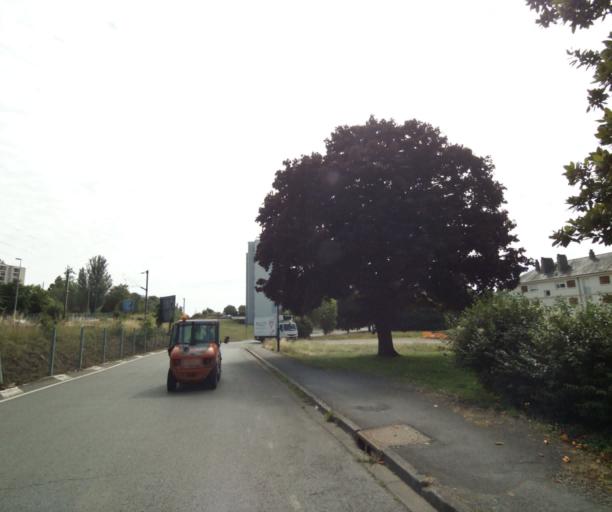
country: FR
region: Pays de la Loire
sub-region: Departement de la Mayenne
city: Laval
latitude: 48.0761
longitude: -0.7819
